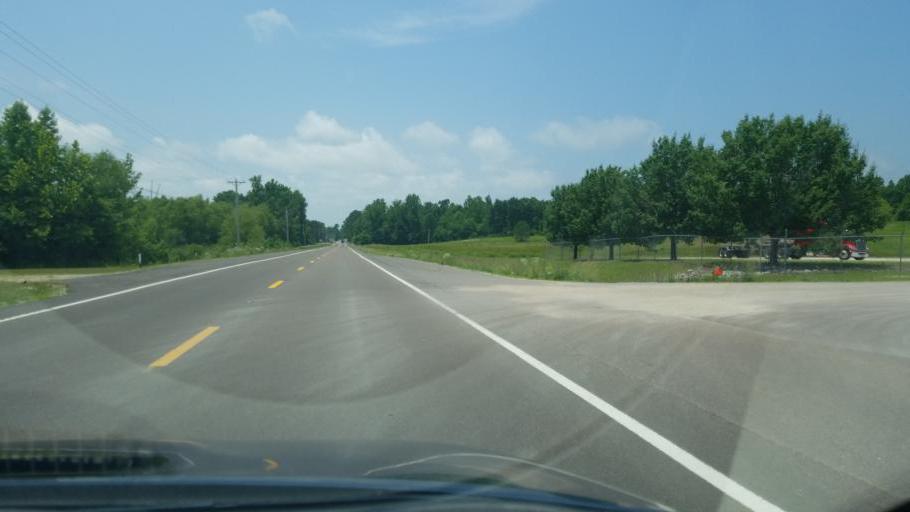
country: US
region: Tennessee
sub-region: Carroll County
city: Bruceton
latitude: 36.0412
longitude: -88.1825
